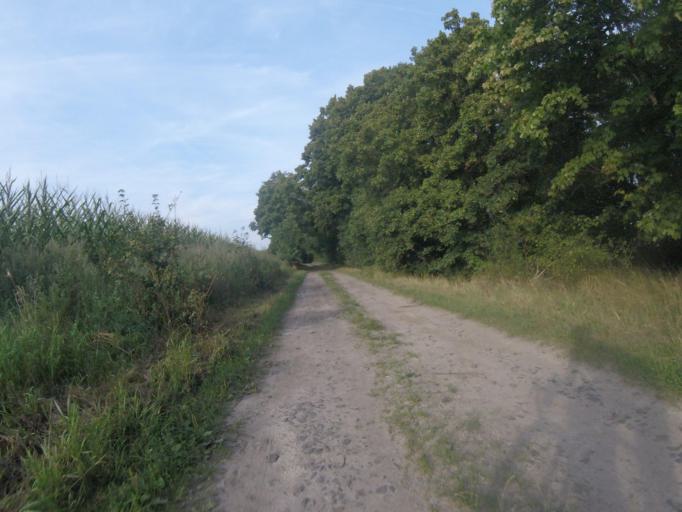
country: DE
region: Berlin
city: Gropiusstadt
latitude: 52.3939
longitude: 13.4651
